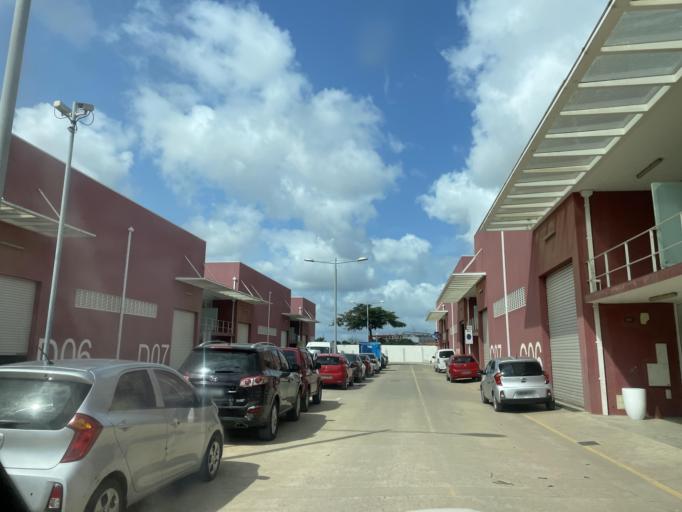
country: AO
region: Luanda
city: Luanda
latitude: -8.9093
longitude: 13.2067
